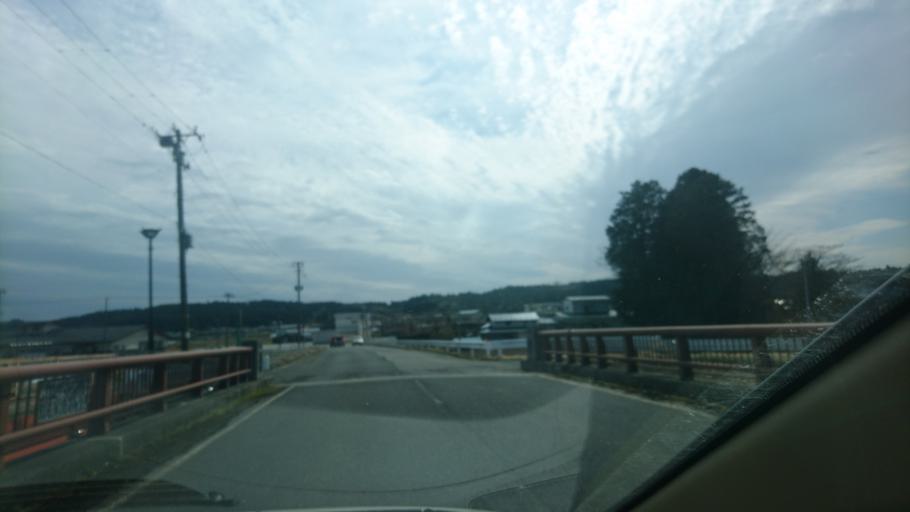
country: JP
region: Miyagi
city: Furukawa
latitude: 38.7411
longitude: 140.9467
